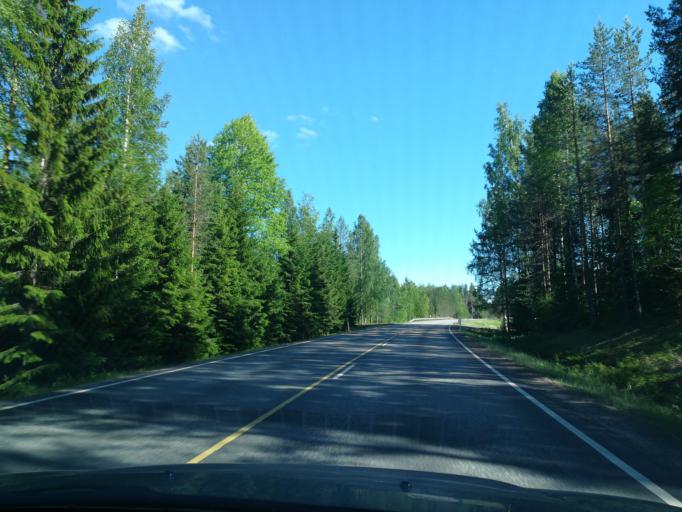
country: FI
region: South Karelia
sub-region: Imatra
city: Ruokolahti
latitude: 61.3860
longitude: 28.6524
